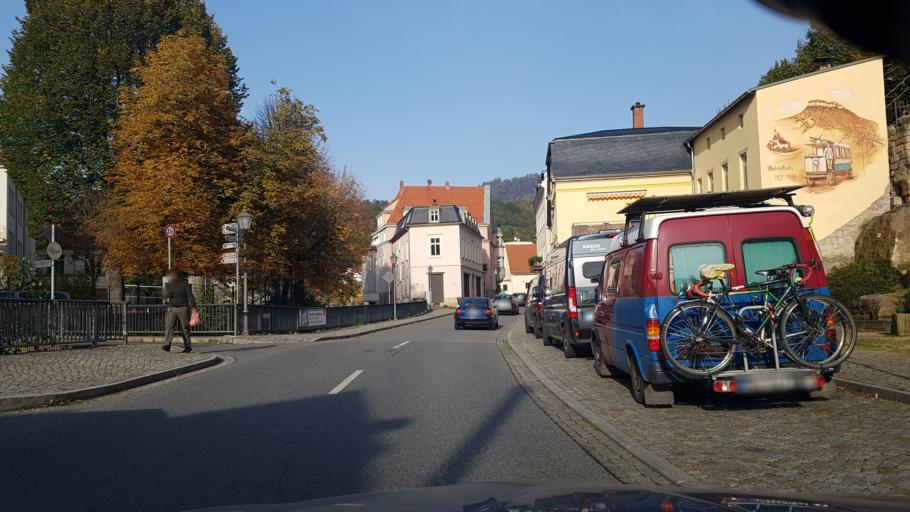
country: DE
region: Saxony
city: Konigstein
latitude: 50.9168
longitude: 14.0725
